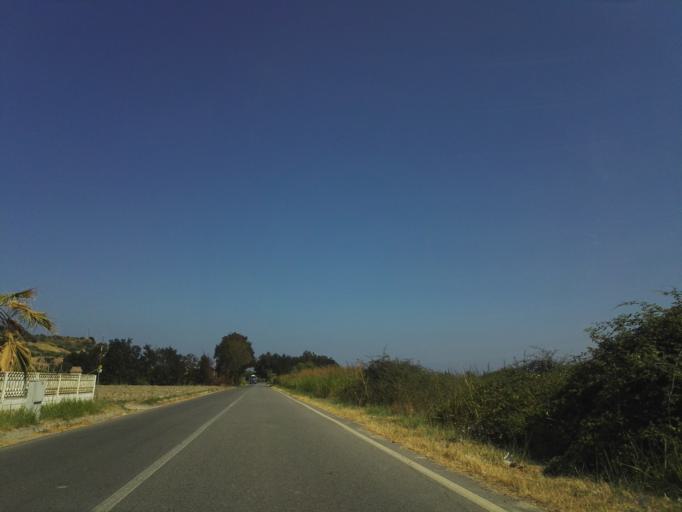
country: IT
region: Calabria
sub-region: Provincia di Reggio Calabria
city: Monasterace Marina
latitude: 38.4369
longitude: 16.5575
